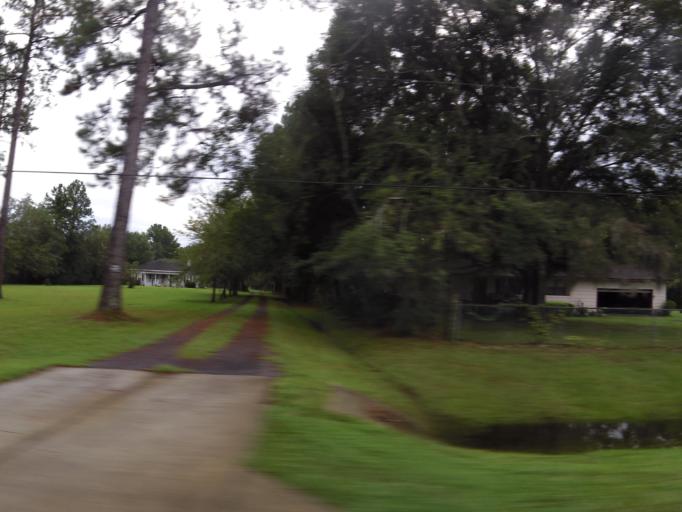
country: US
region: Florida
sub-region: Duval County
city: Baldwin
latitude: 30.3941
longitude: -81.9456
